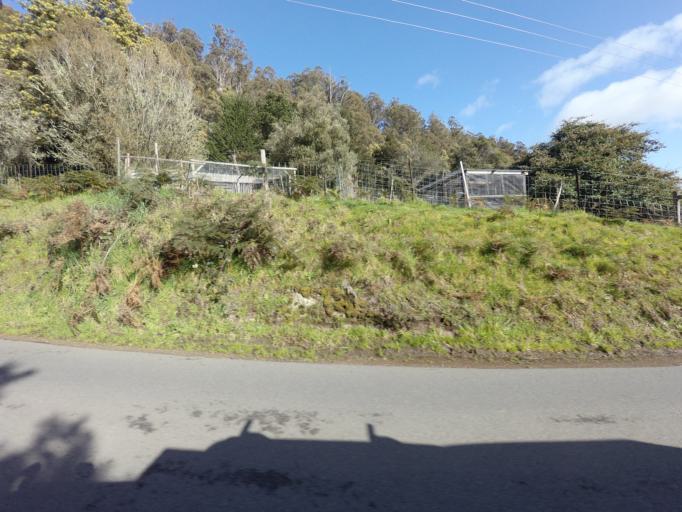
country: AU
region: Tasmania
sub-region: Huon Valley
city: Geeveston
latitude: -43.2480
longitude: 146.9909
